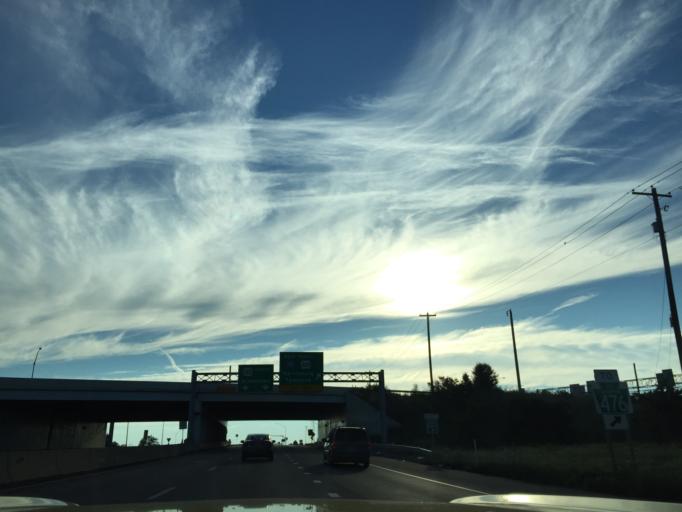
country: US
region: Pennsylvania
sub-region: Lehigh County
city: Wescosville
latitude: 40.5718
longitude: -75.5408
